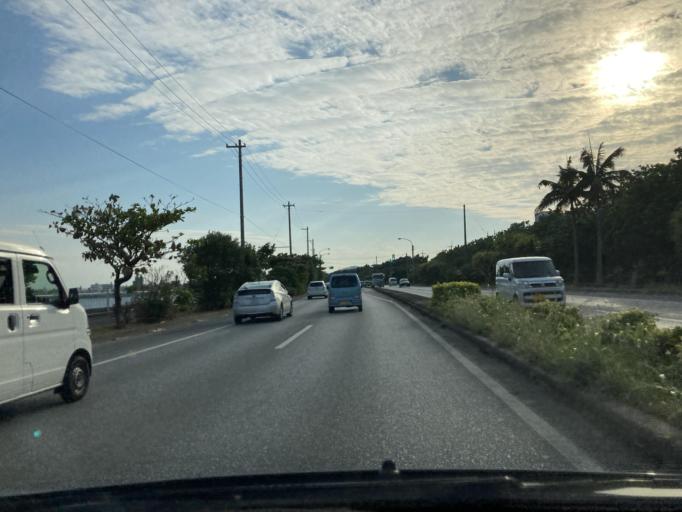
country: JP
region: Okinawa
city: Okinawa
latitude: 26.3298
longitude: 127.8366
